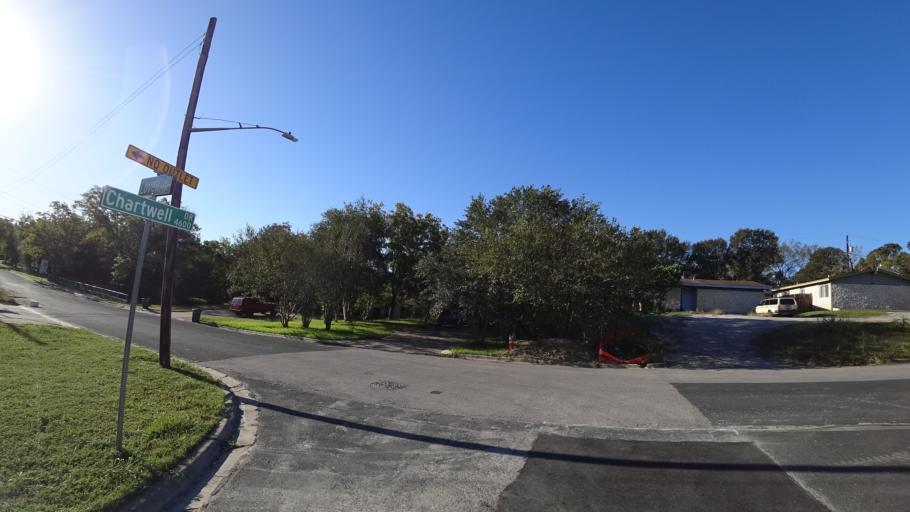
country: US
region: Texas
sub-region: Travis County
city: Austin
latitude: 30.2920
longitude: -97.6880
